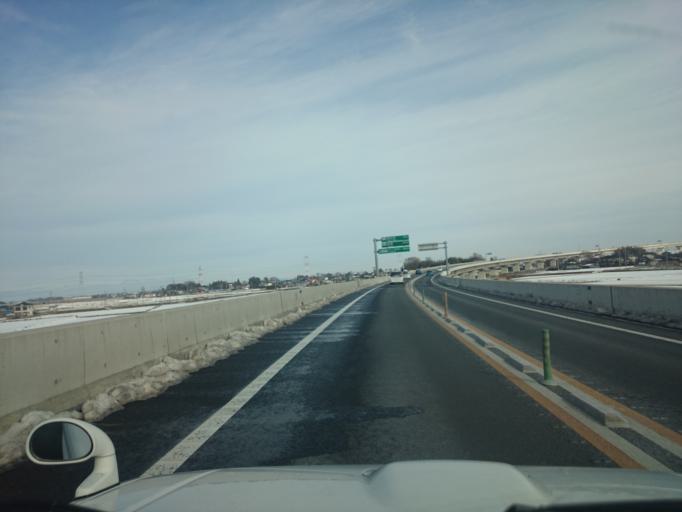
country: JP
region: Ibaraki
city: Sakai
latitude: 36.1065
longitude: 139.7567
